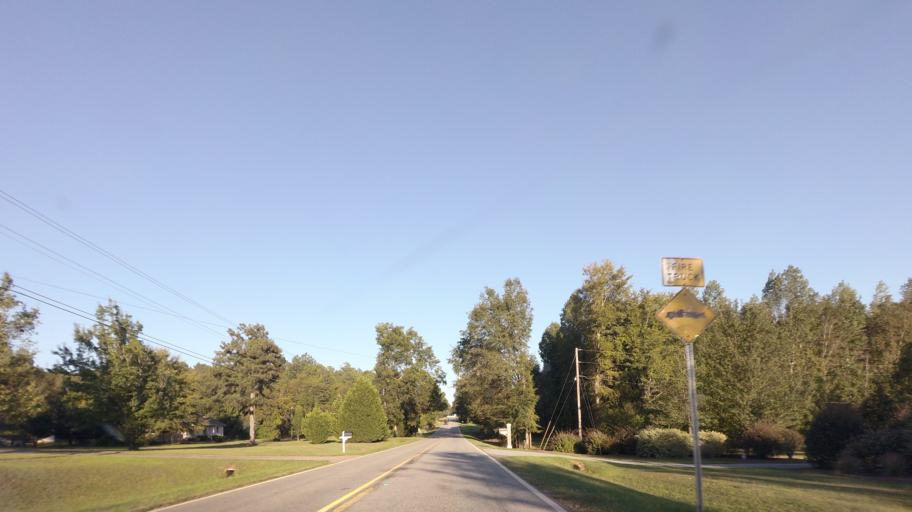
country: US
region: Georgia
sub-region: Spalding County
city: East Griffin
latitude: 33.2901
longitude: -84.1794
